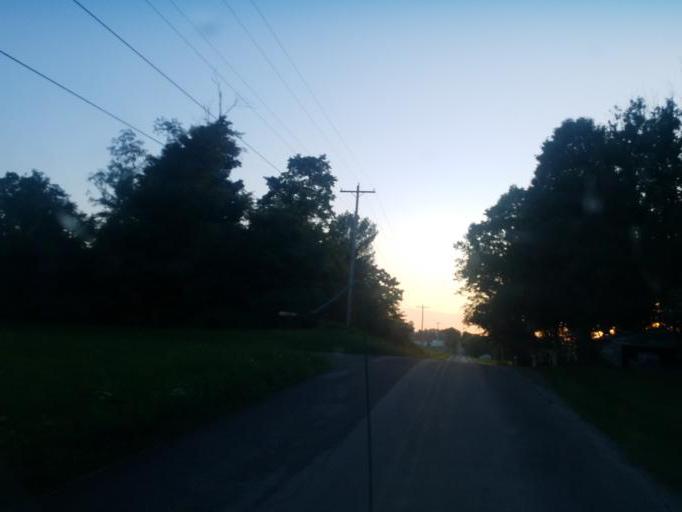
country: US
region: Ohio
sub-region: Knox County
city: Fredericktown
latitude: 40.4964
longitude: -82.6248
